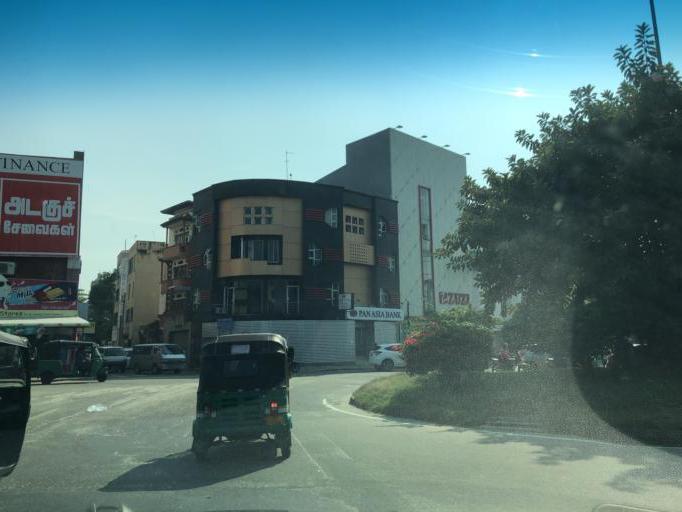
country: LK
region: Western
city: Colombo
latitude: 6.9475
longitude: 79.8620
